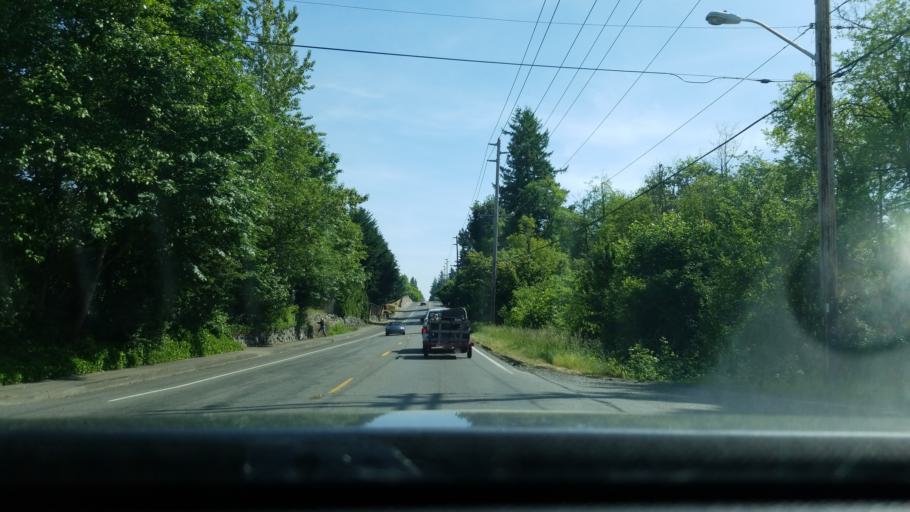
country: US
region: Washington
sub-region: Pierce County
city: Puyallup
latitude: 47.1736
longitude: -122.3043
